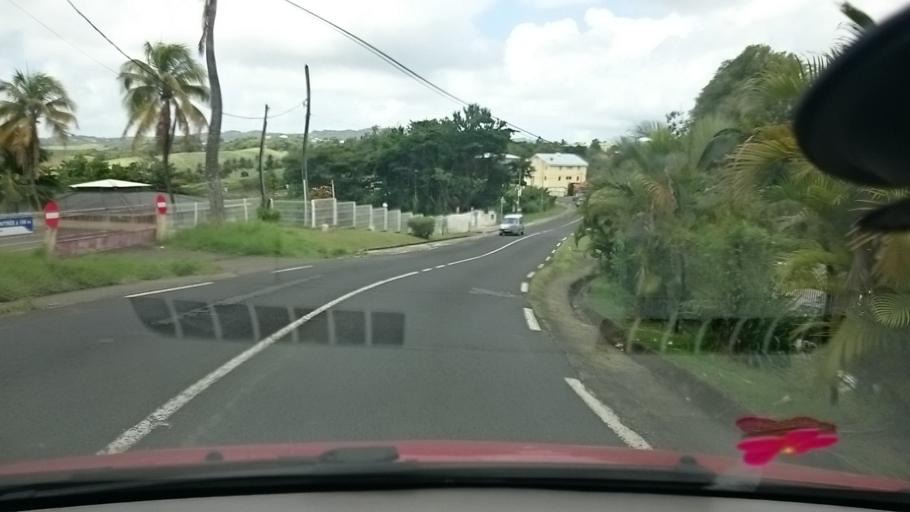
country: MQ
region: Martinique
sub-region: Martinique
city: La Trinite
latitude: 14.7375
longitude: -60.9529
